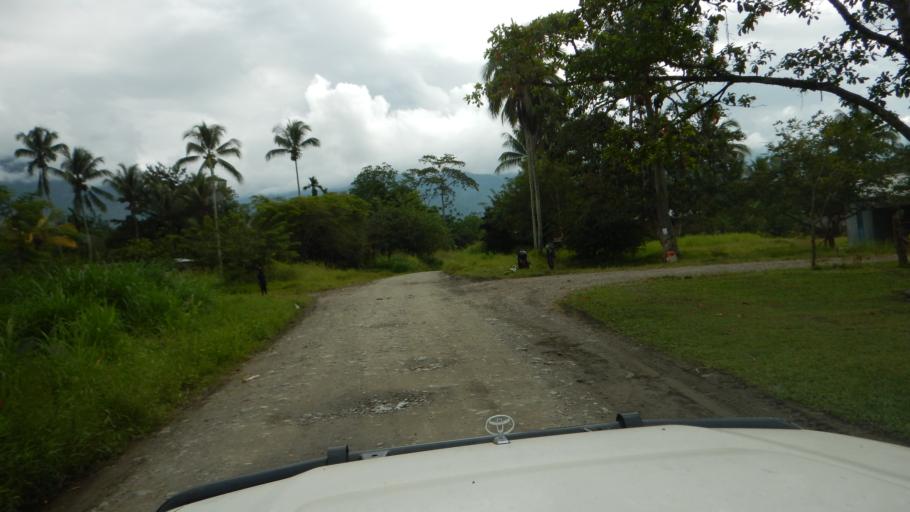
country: PG
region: Northern Province
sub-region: Sohe
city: Kokoda
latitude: -8.9164
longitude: 147.7887
